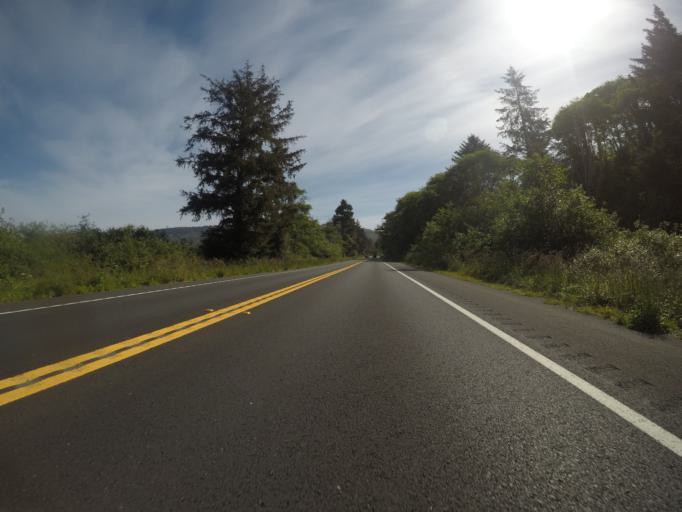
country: US
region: California
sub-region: Humboldt County
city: Westhaven-Moonstone
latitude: 41.2849
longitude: -124.0875
